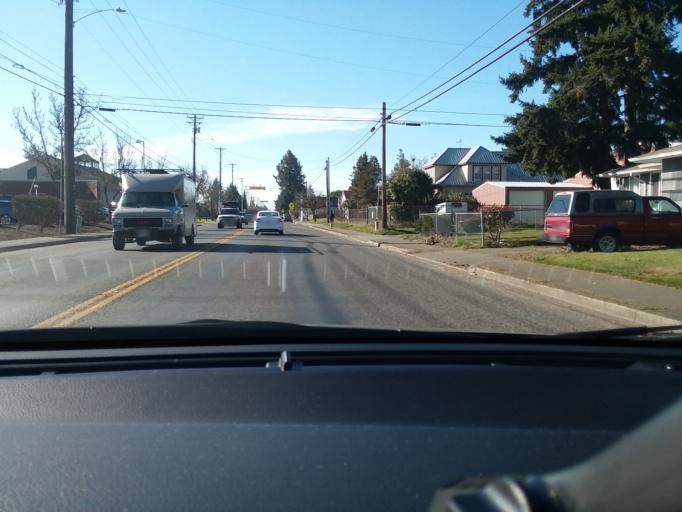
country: US
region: Washington
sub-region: Pierce County
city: Midland
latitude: 47.2098
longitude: -122.4210
